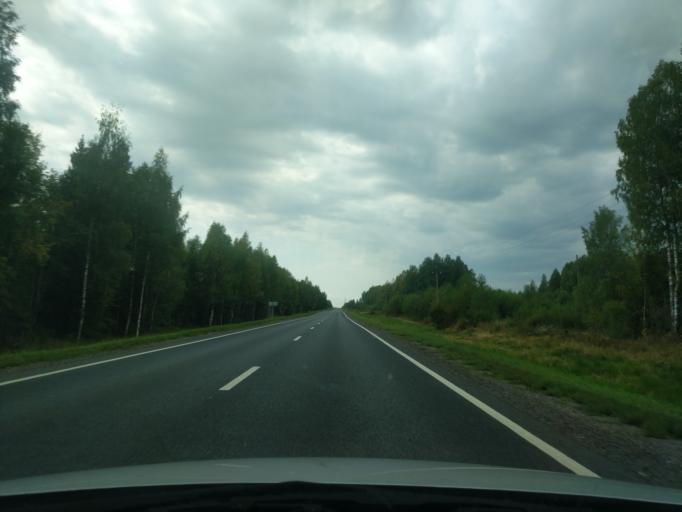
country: RU
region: Kostroma
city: Manturovo
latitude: 58.1529
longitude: 44.3776
